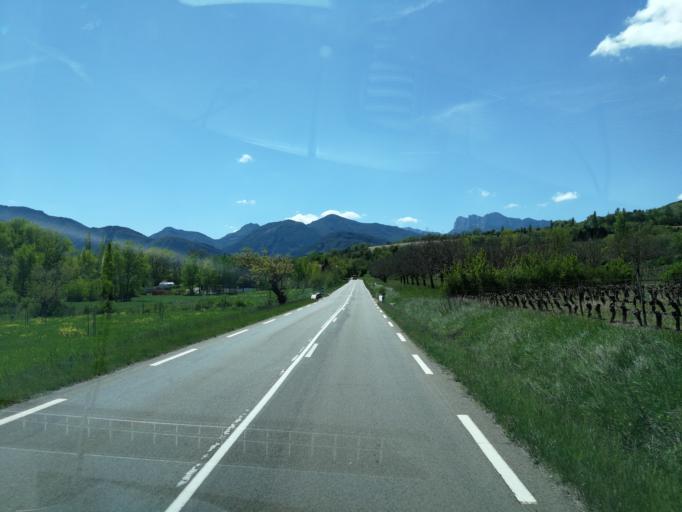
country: FR
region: Rhone-Alpes
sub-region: Departement de la Drome
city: Die
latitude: 44.7316
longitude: 5.2675
